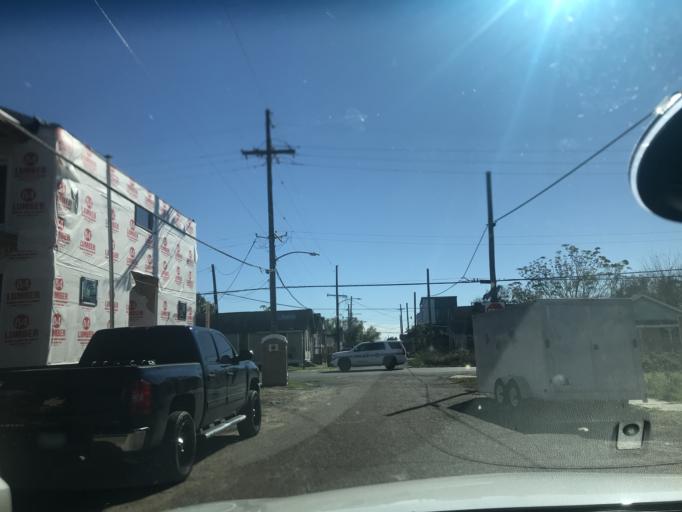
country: US
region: Louisiana
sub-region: Orleans Parish
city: New Orleans
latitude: 29.9508
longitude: -90.0984
